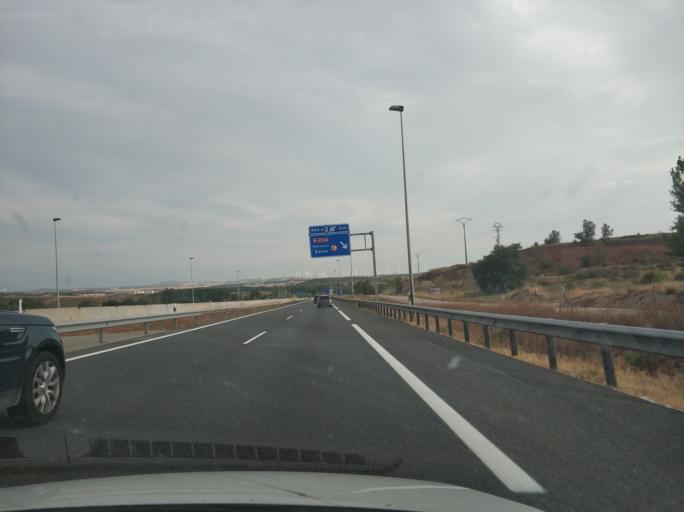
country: ES
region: Castille and Leon
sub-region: Provincia de Burgos
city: Saldana de Burgos
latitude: 42.2738
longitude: -3.7022
